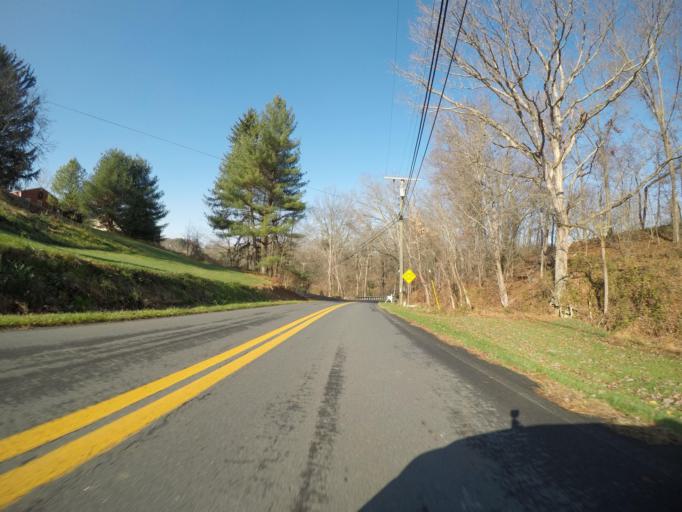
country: US
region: Maryland
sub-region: Baltimore County
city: Reisterstown
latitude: 39.5316
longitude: -76.8609
